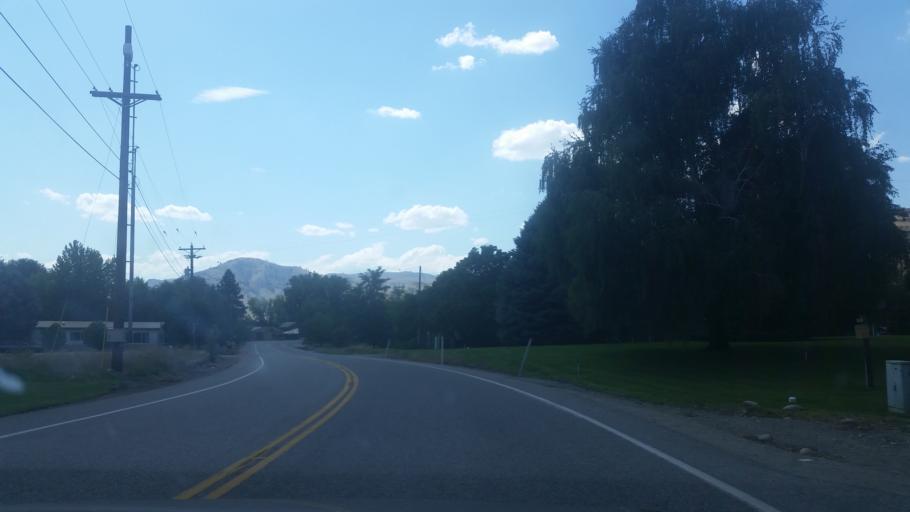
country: US
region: Washington
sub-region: Okanogan County
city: Okanogan
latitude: 48.2847
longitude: -119.7032
